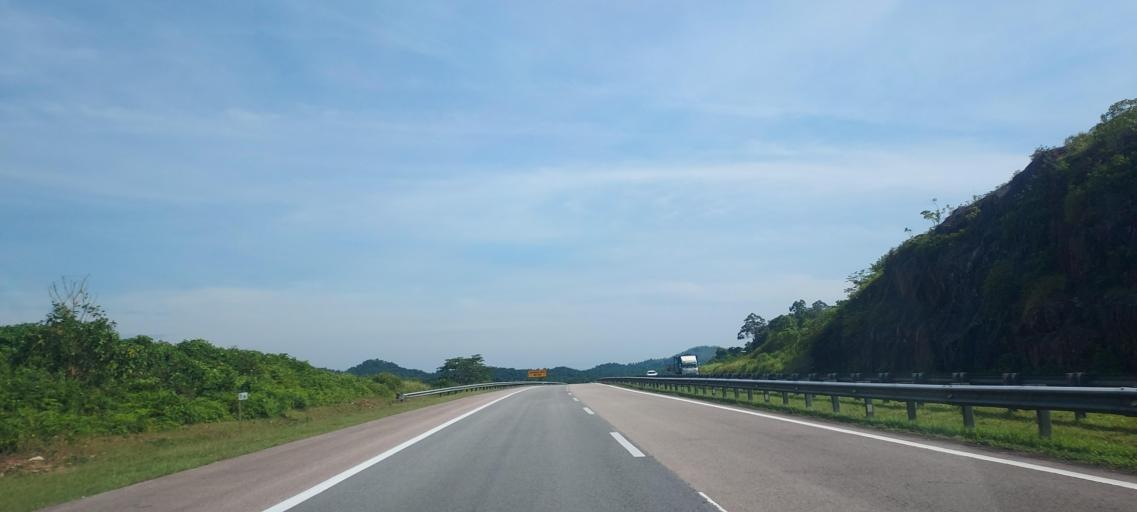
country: MY
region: Terengganu
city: Marang
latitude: 4.9526
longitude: 103.0858
